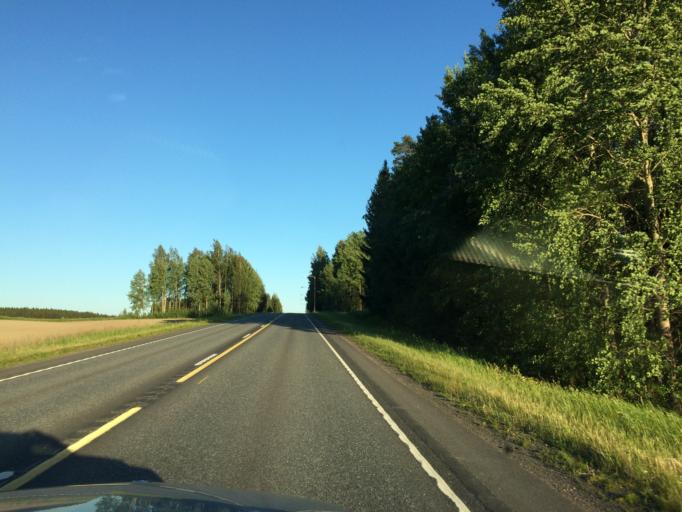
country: FI
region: Haeme
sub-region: Haemeenlinna
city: Tervakoski
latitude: 60.7927
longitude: 24.6725
